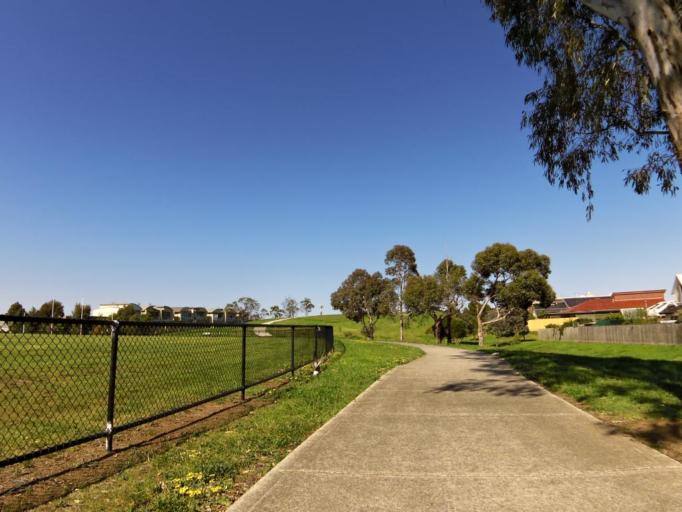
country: AU
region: Victoria
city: Plenty
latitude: -37.6841
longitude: 145.1152
